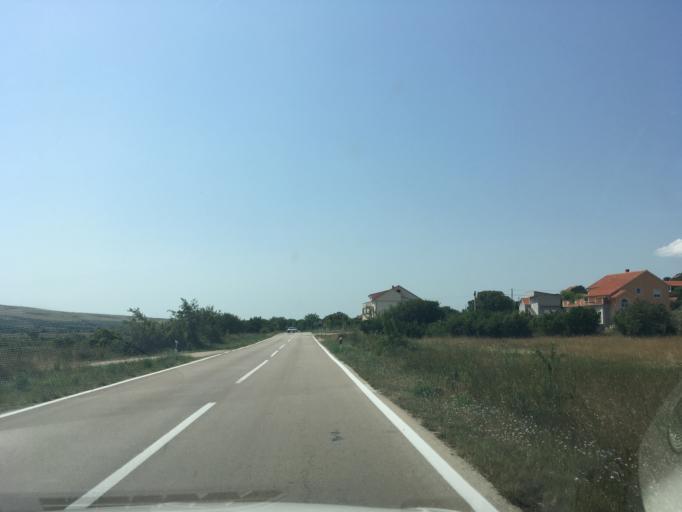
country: HR
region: Zadarska
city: Benkovac
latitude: 43.9657
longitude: 15.7280
